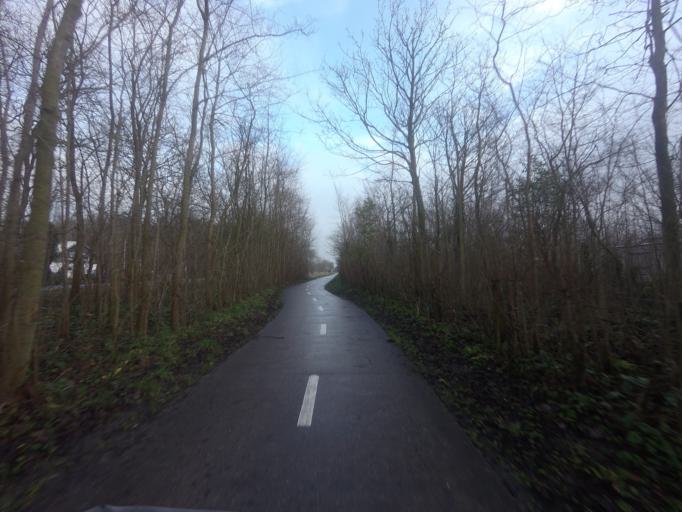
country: NL
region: North Holland
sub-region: Gemeente Texel
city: Den Burg
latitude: 53.1566
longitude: 4.8573
